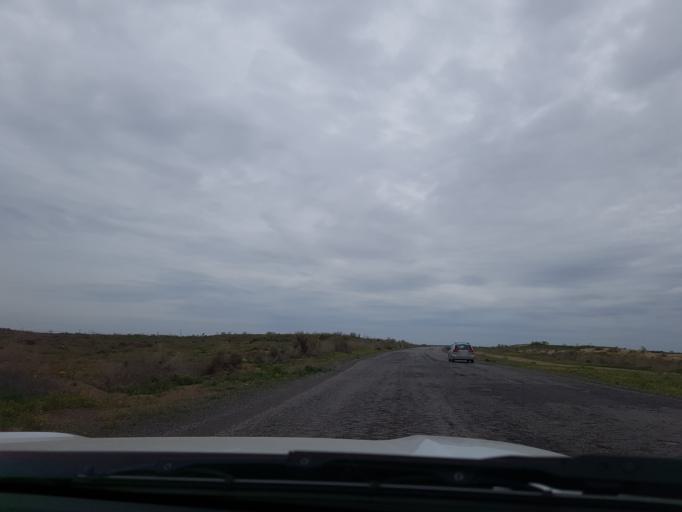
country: TM
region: Mary
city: Bayramaly
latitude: 38.0320
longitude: 62.7508
